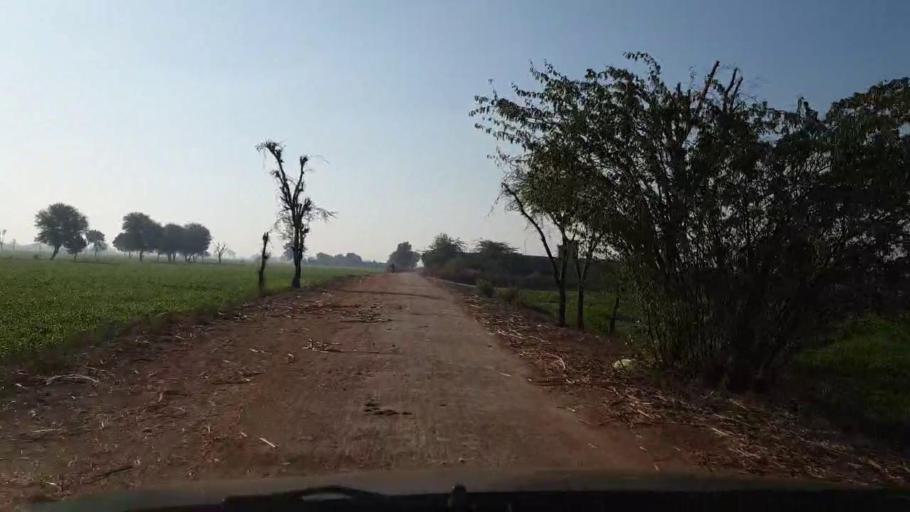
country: PK
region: Sindh
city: Jhol
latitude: 25.9333
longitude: 68.8654
